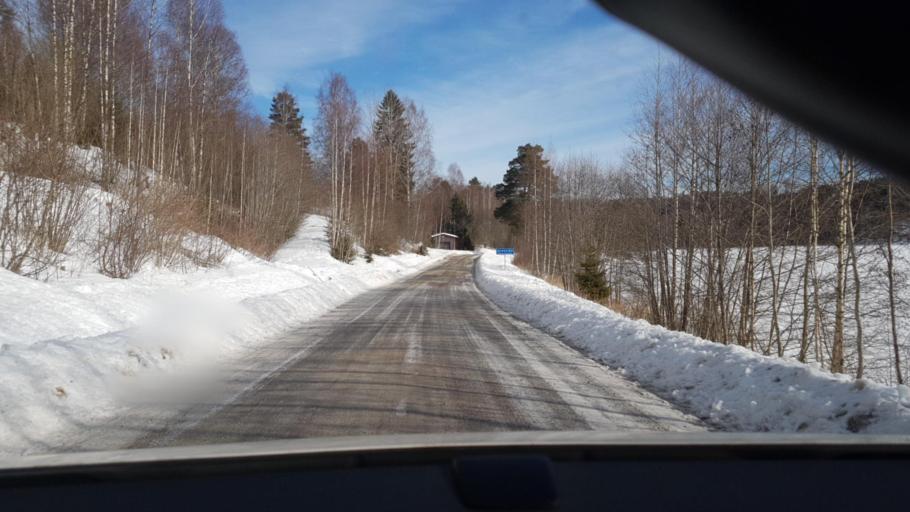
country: NO
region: Hedmark
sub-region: Eidskog
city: Skotterud
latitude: 59.8850
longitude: 11.9790
